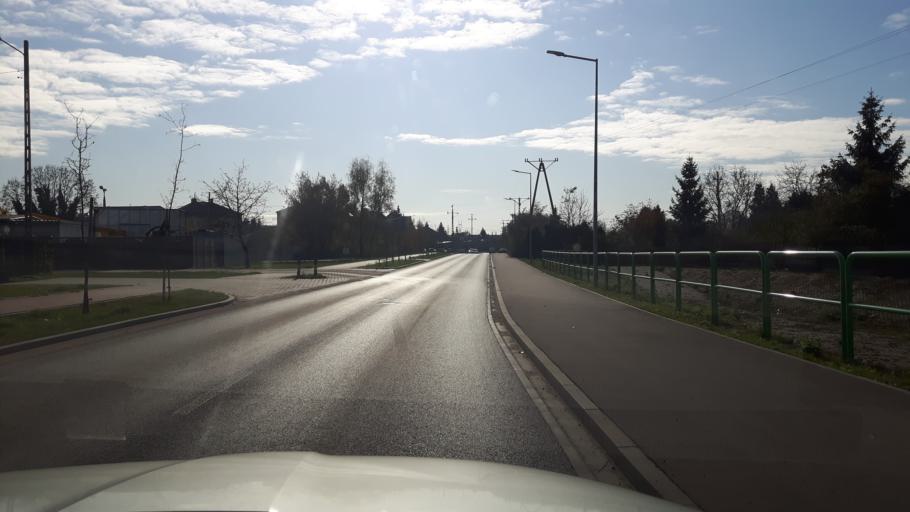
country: PL
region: Masovian Voivodeship
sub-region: Powiat wolominski
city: Zabki
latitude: 52.2944
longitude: 21.1003
